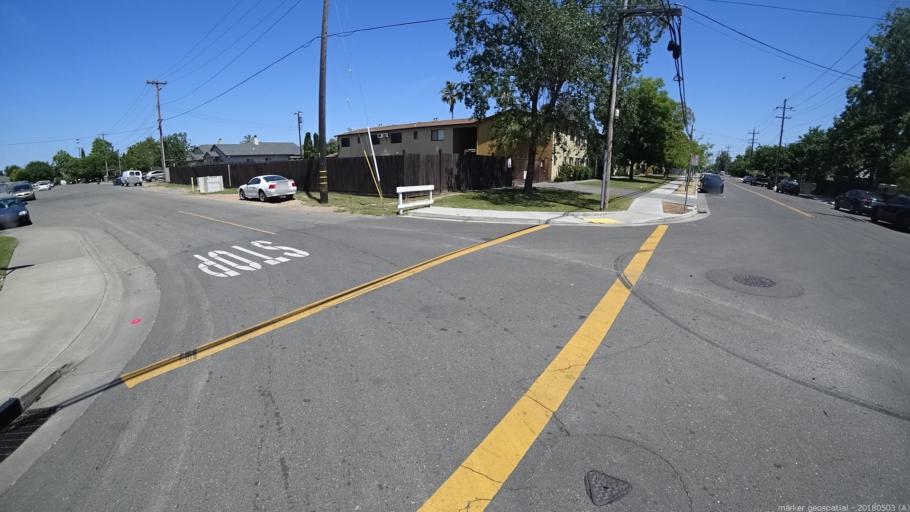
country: US
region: California
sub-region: Sacramento County
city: Arden-Arcade
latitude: 38.6400
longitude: -121.4177
